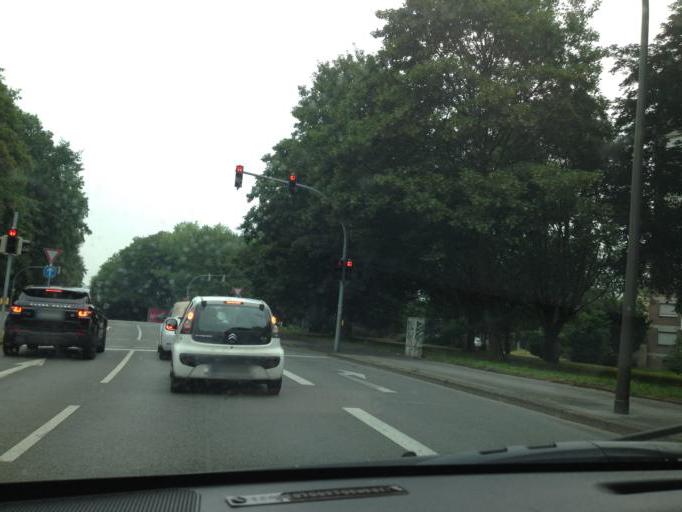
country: DE
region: North Rhine-Westphalia
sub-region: Regierungsbezirk Arnsberg
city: Dortmund
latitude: 51.4794
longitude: 7.4598
